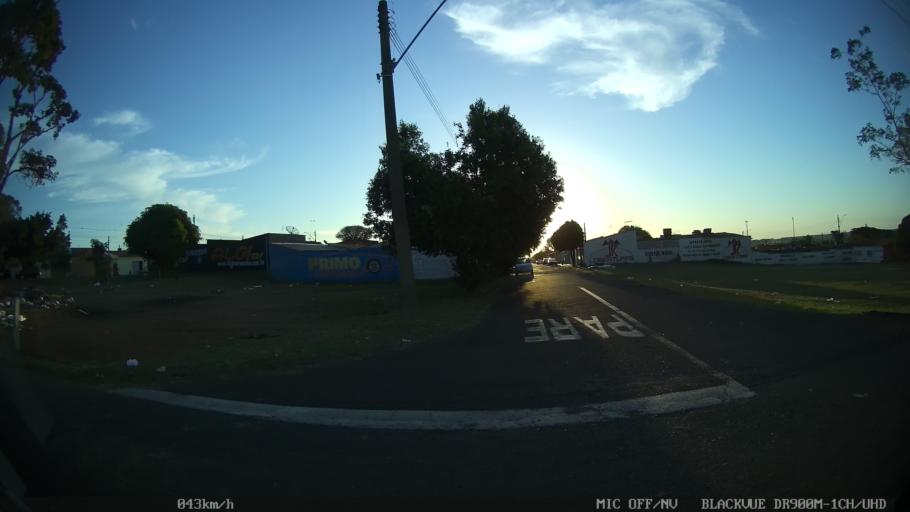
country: BR
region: Sao Paulo
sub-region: Franca
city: Franca
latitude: -20.5001
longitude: -47.4078
